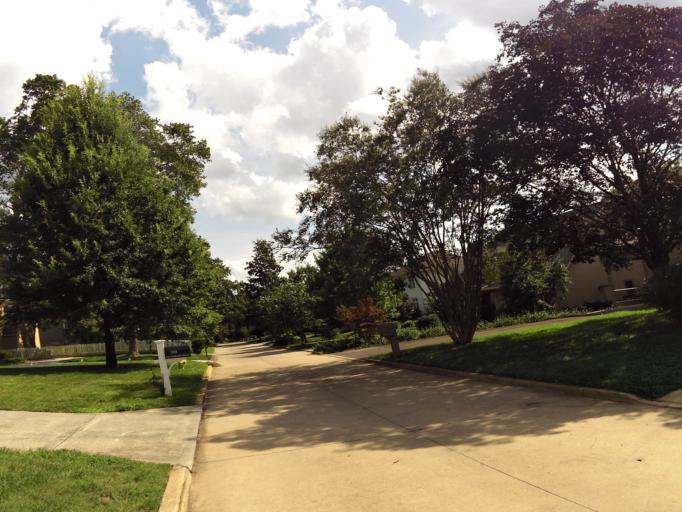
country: US
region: Tennessee
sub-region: Knox County
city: Knoxville
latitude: 35.9358
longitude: -83.9651
